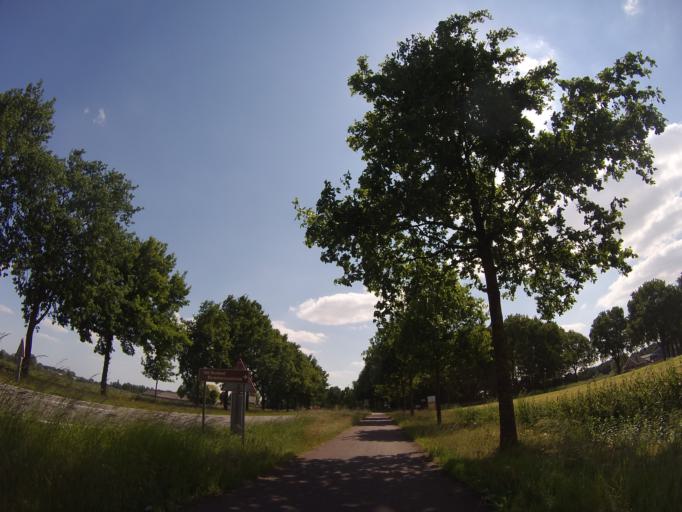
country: NL
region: Gelderland
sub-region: Gemeente Barneveld
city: Barneveld
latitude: 52.1603
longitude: 5.5704
